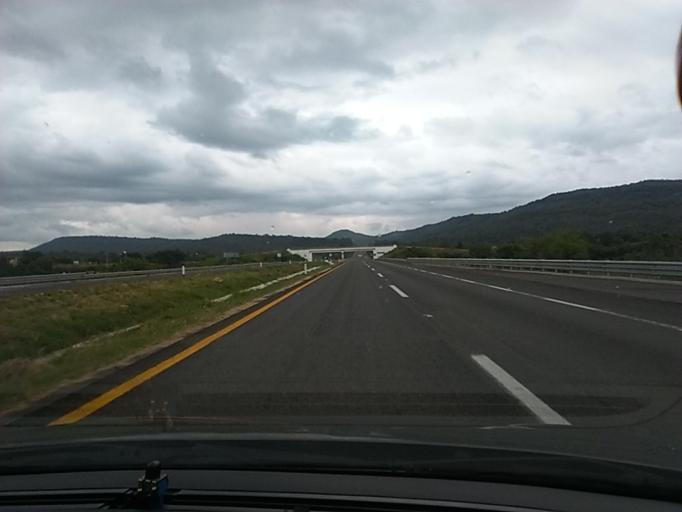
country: MX
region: Jalisco
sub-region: Zapotlanejo
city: La Mezquitera
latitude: 20.5447
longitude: -103.0291
